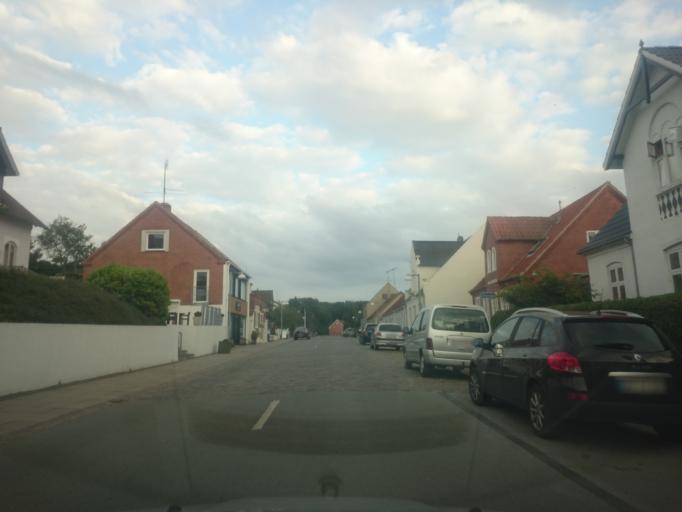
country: DK
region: South Denmark
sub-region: Nyborg Kommune
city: Nyborg
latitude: 55.1346
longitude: 10.9037
